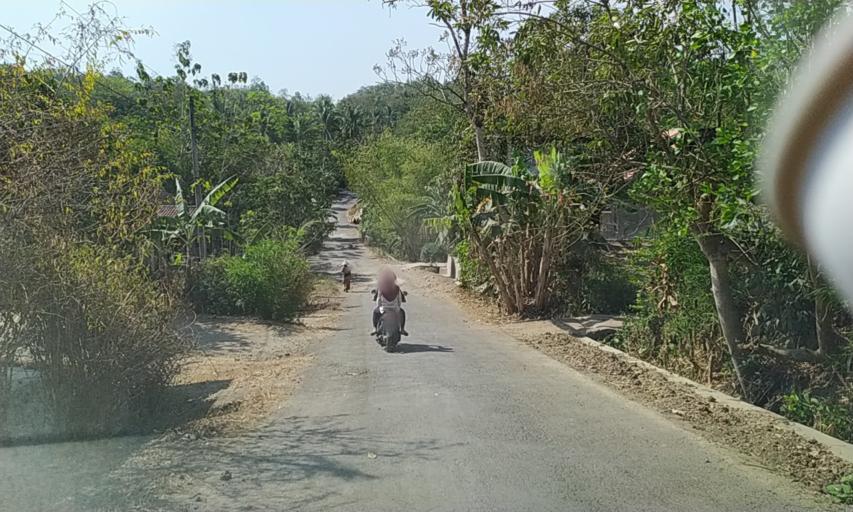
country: ID
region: Central Java
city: Ciloning
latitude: -7.4826
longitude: 108.8572
